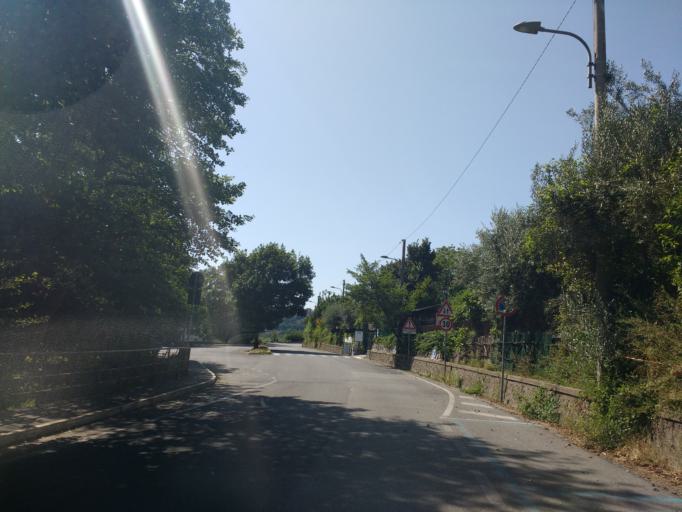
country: IT
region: Latium
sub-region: Citta metropolitana di Roma Capitale
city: Castel Gandolfo
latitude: 41.7590
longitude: 12.6692
